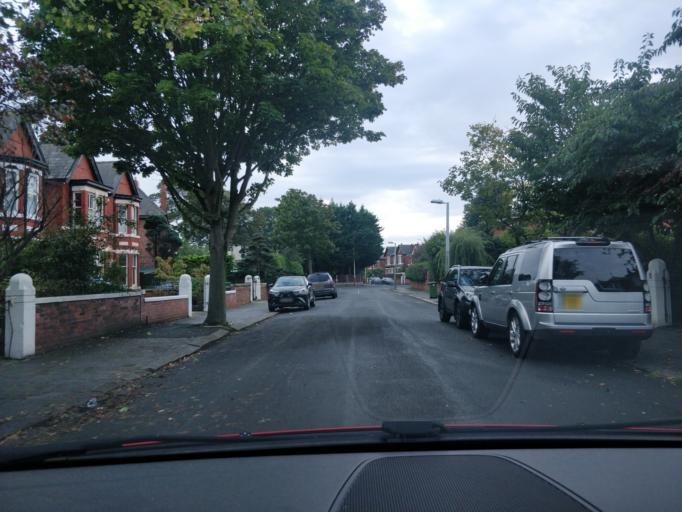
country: GB
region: England
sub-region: Sefton
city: Southport
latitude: 53.6445
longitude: -2.9812
